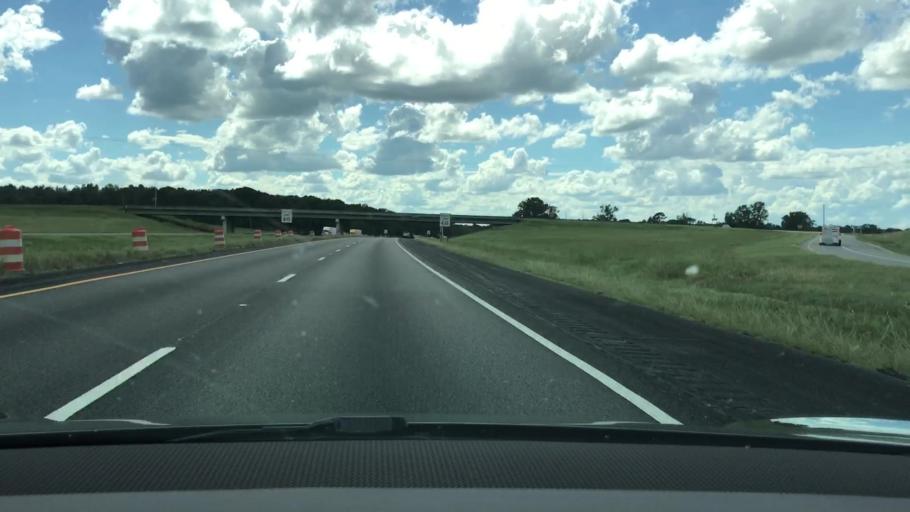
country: US
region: Alabama
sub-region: Elmore County
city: Tallassee
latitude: 32.4288
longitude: -85.8967
